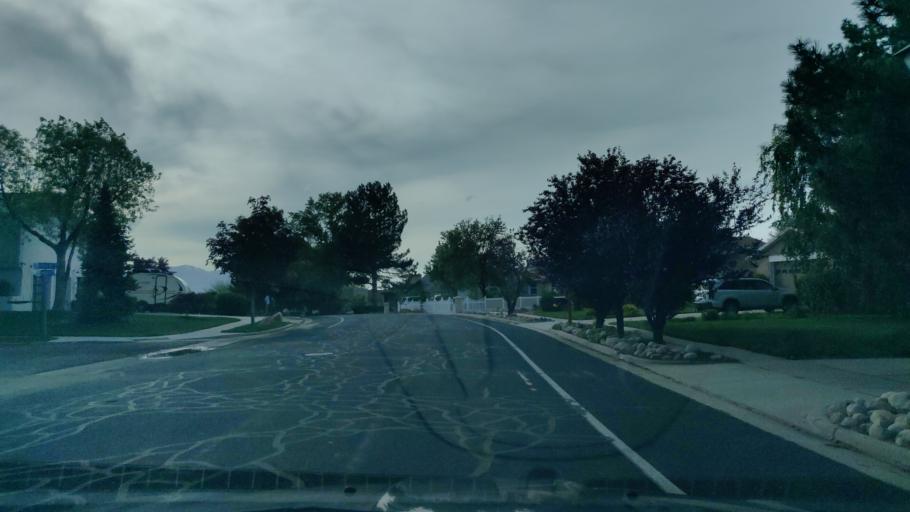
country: US
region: Utah
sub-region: Salt Lake County
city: Little Cottonwood Creek Valley
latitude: 40.6162
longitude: -111.8369
